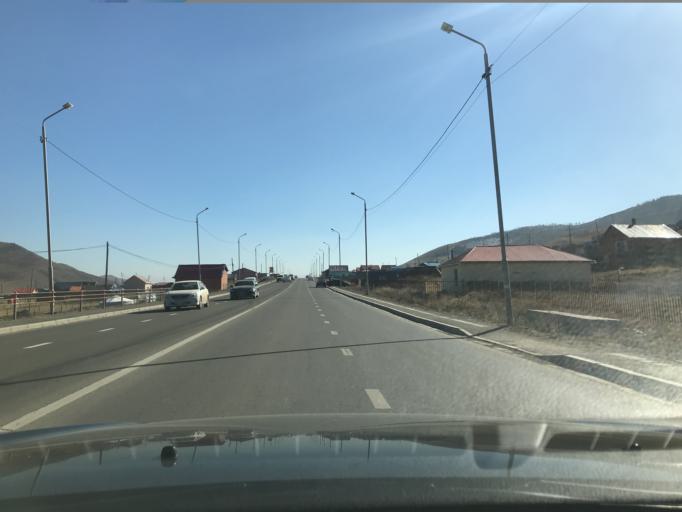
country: MN
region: Ulaanbaatar
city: Ulaanbaatar
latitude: 48.0427
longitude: 106.9033
